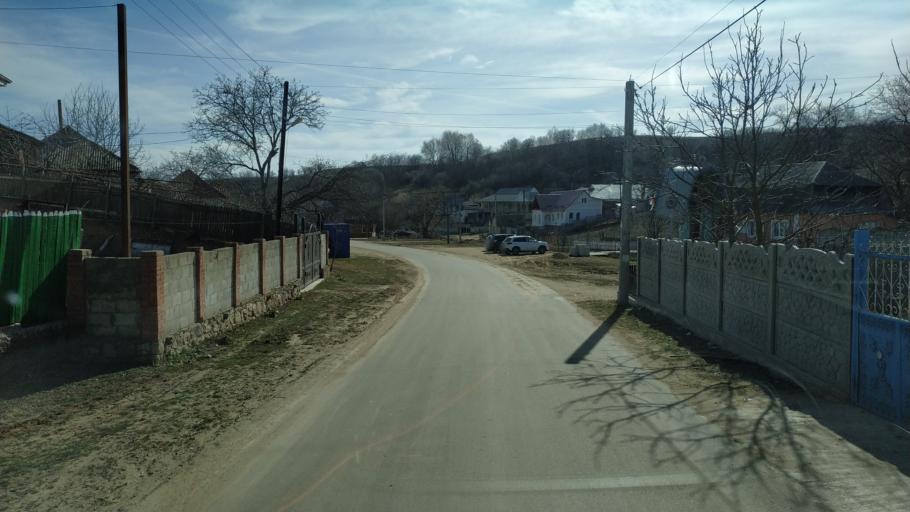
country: MD
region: Nisporeni
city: Nisporeni
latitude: 47.0953
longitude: 28.2988
